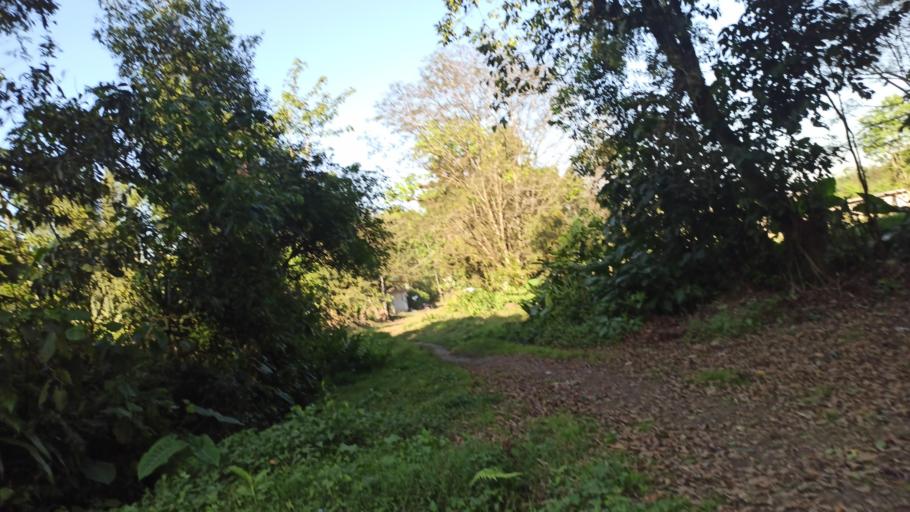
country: MX
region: Veracruz
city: Atzacan
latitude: 18.9093
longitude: -97.0916
